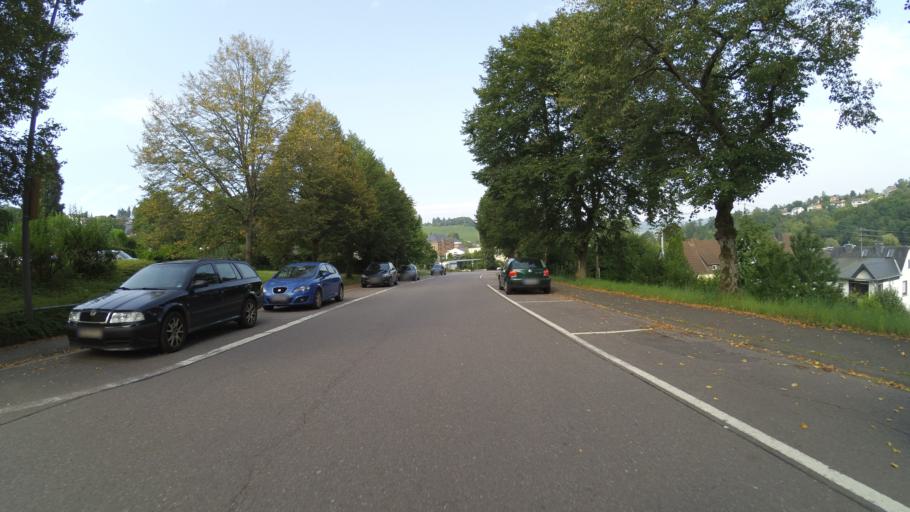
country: DE
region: Rheinland-Pfalz
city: Saarburg
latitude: 49.6033
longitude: 6.5392
